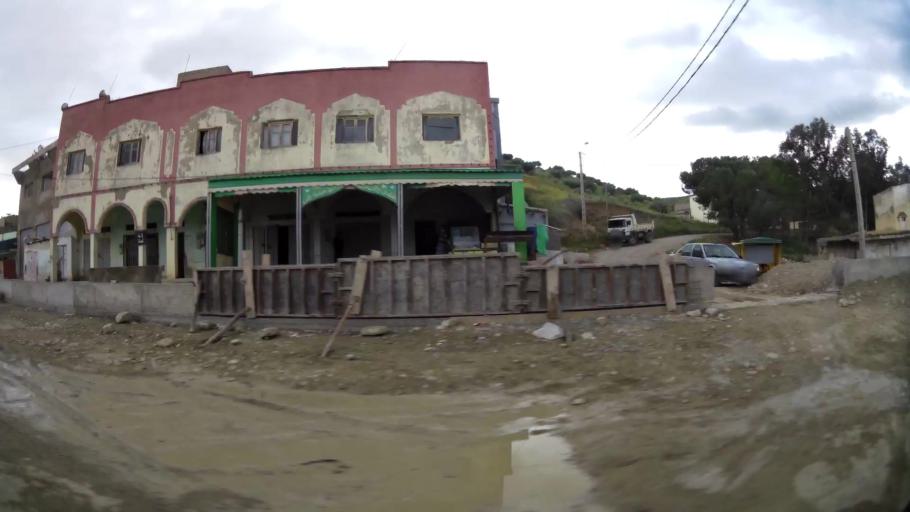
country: MA
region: Taza-Al Hoceima-Taounate
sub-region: Taza
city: Taza
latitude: 34.3460
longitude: -3.9252
